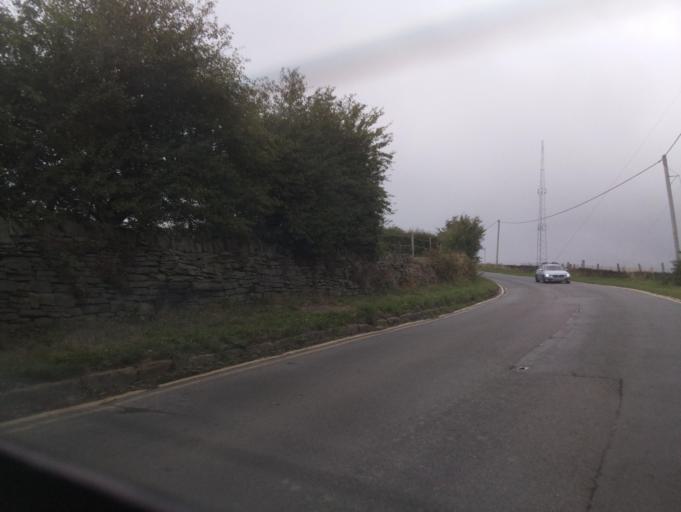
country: GB
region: England
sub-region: Kirklees
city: Shelley
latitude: 53.6112
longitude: -1.6706
